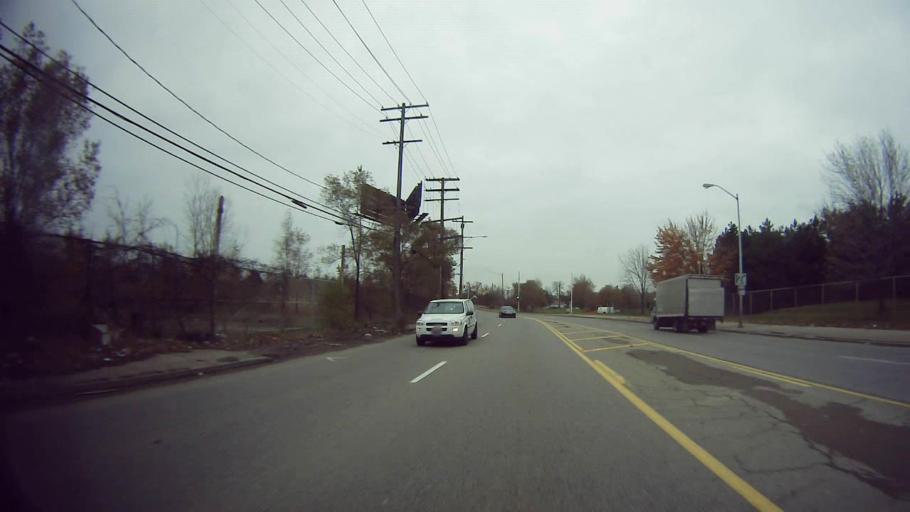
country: US
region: Michigan
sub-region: Wayne County
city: Hamtramck
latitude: 42.3803
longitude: -83.0350
